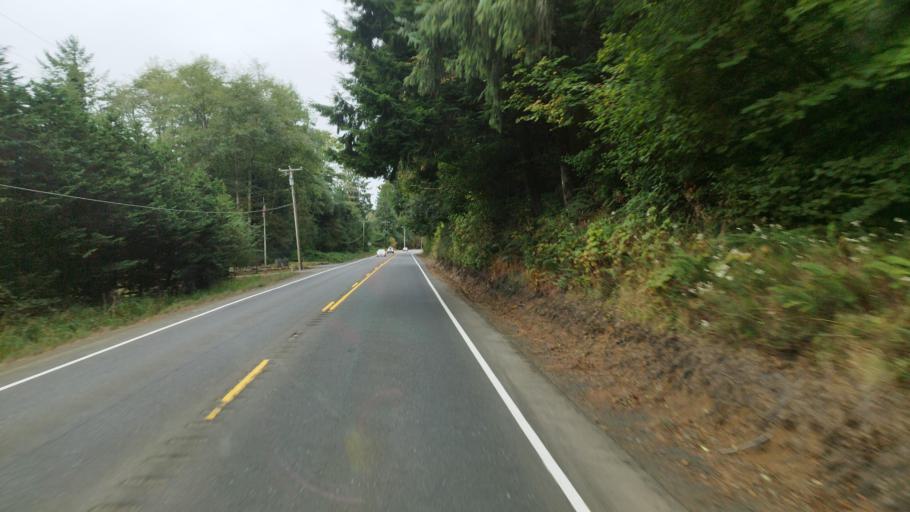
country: US
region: Oregon
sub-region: Clatsop County
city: Seaside
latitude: 45.9252
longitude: -123.8968
